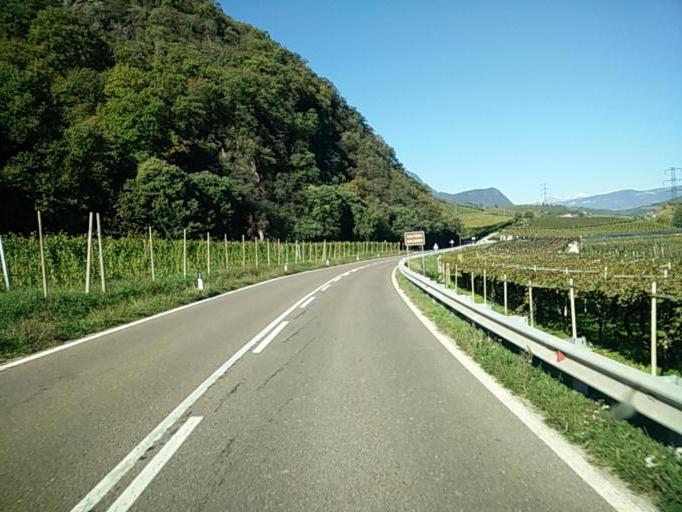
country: IT
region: Trentino-Alto Adige
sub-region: Bolzano
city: Termeno
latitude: 46.3666
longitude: 11.2515
